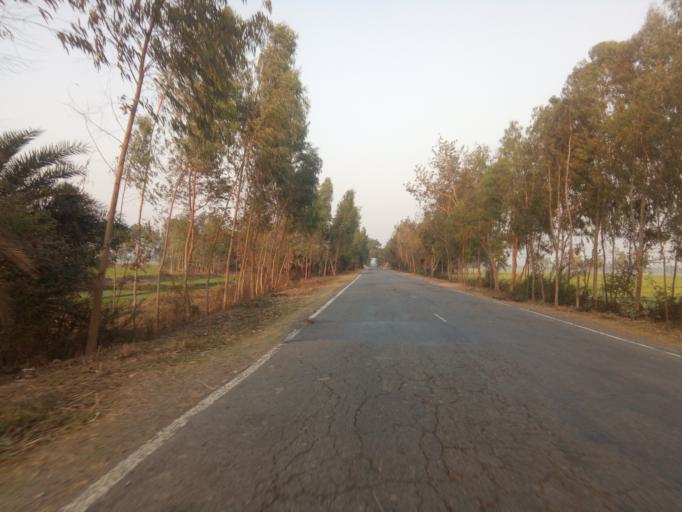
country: BD
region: Rajshahi
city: Bogra
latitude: 24.5761
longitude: 89.2201
